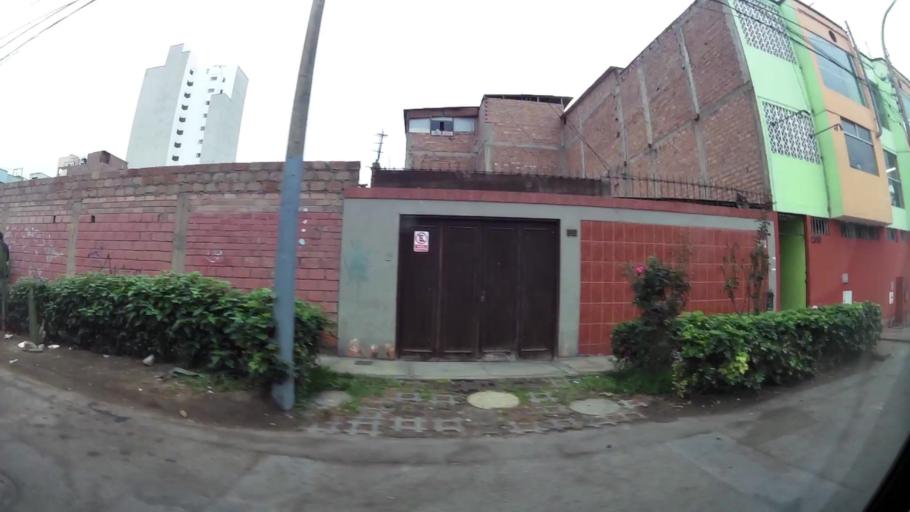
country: PE
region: Callao
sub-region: Callao
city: Callao
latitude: -12.0876
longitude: -77.0852
